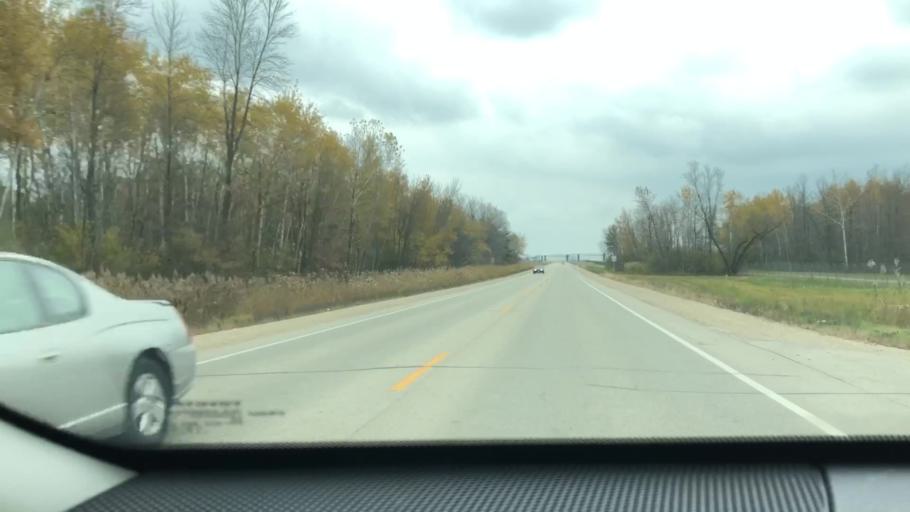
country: US
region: Wisconsin
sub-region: Brown County
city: Oneida
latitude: 44.4985
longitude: -88.1434
